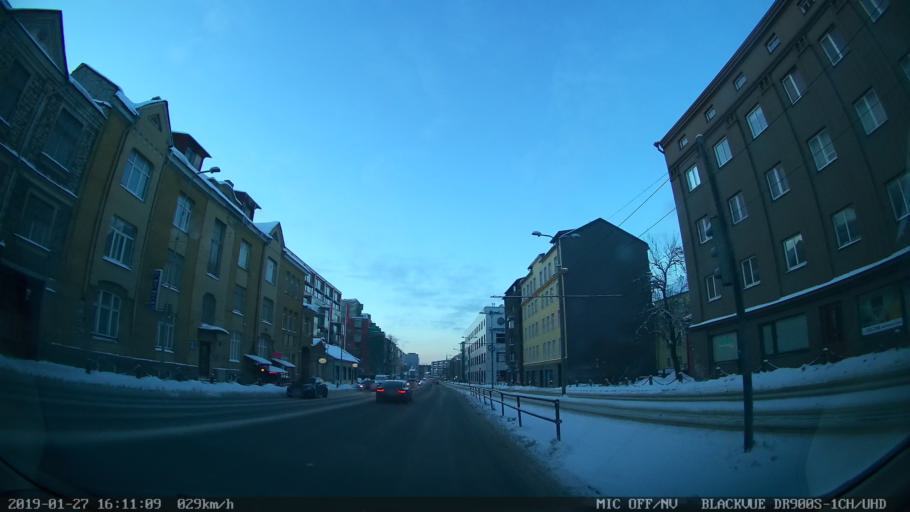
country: EE
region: Harju
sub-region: Tallinna linn
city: Tallinn
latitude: 59.4288
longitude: 24.7753
